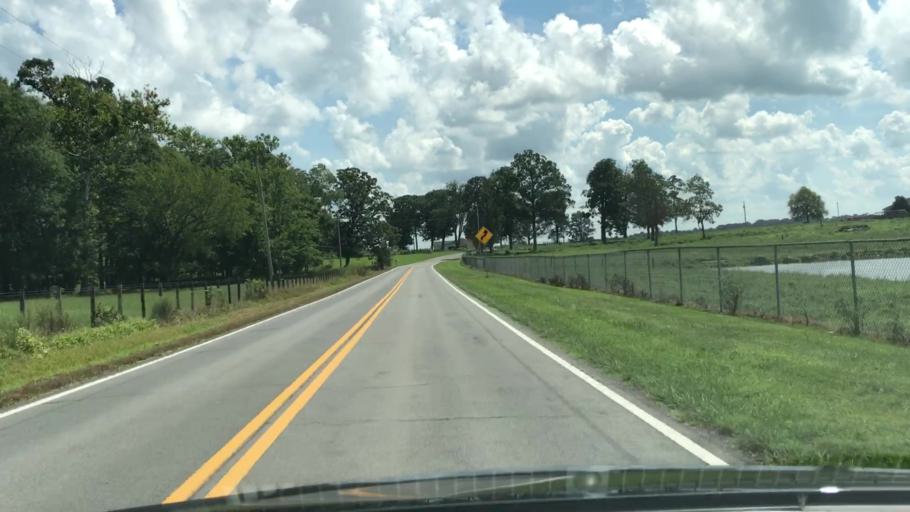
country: US
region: Tennessee
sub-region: Robertson County
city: Springfield
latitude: 36.5919
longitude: -86.8996
